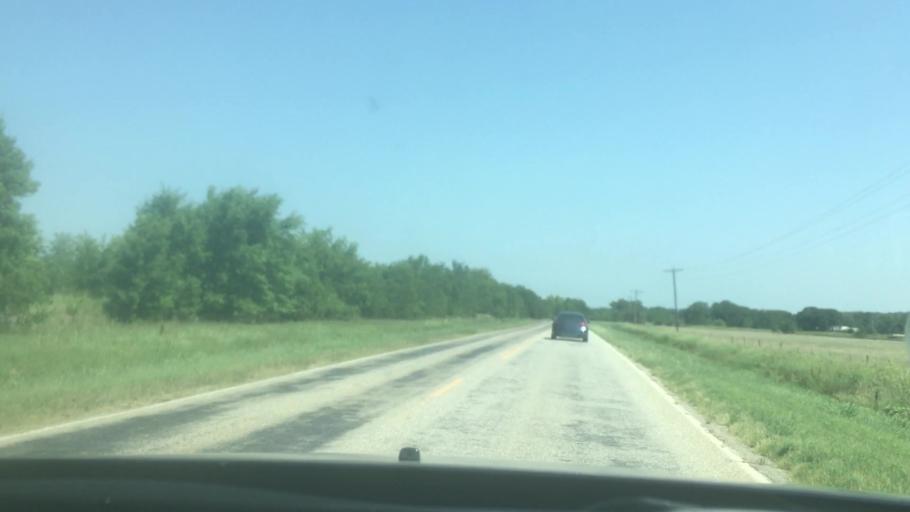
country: US
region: Oklahoma
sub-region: Johnston County
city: Tishomingo
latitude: 34.3477
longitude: -96.4236
